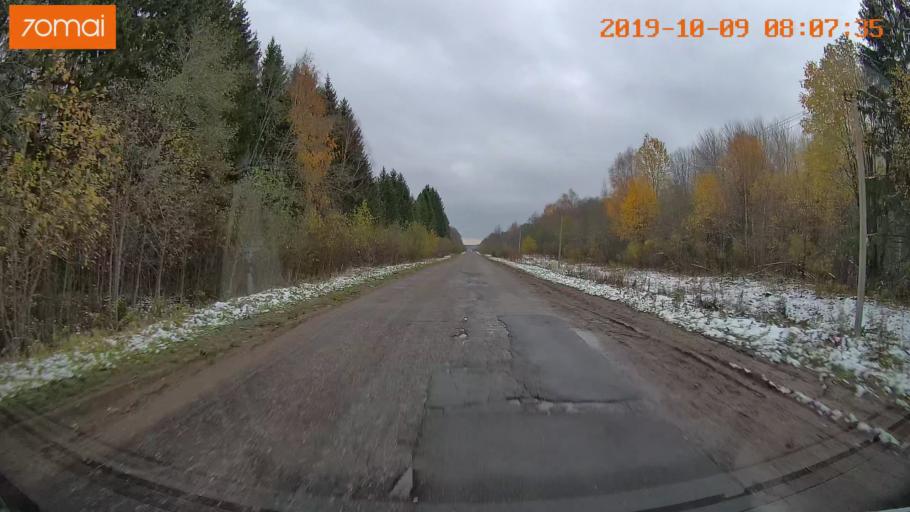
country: RU
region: Jaroslavl
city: Kukoboy
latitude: 58.6987
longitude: 40.0826
